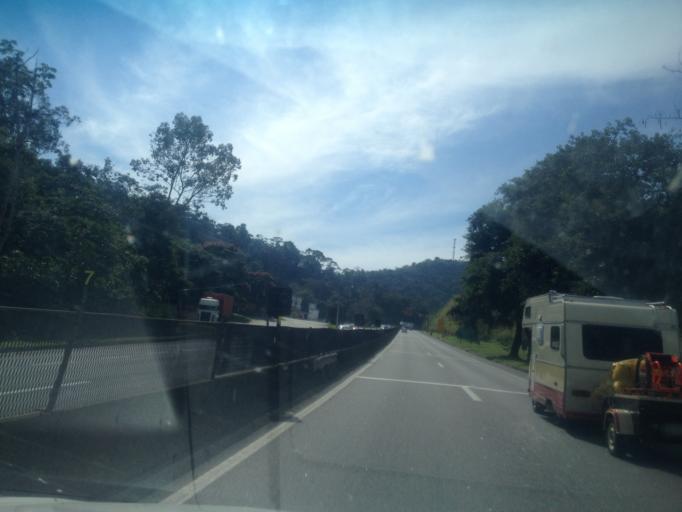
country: BR
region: Rio de Janeiro
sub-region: Pirai
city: Pirai
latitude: -22.6686
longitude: -43.8522
